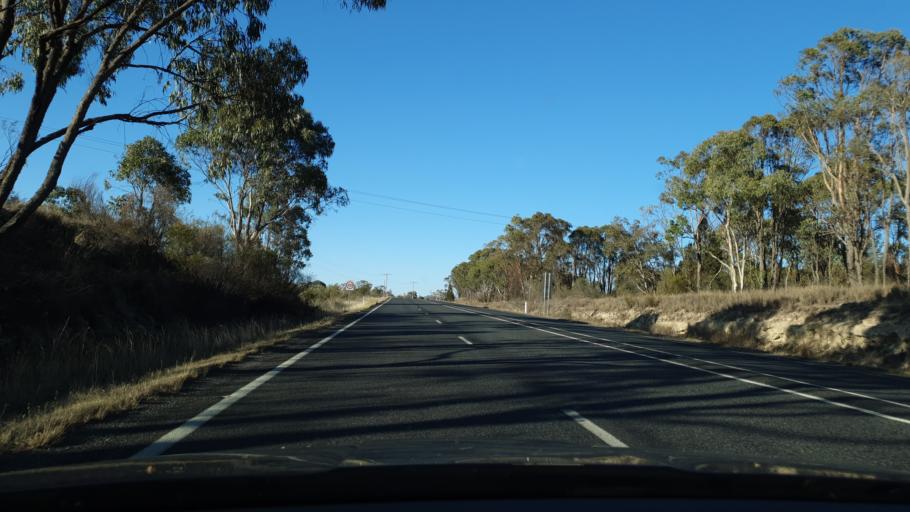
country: AU
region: Queensland
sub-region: Southern Downs
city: Stanthorpe
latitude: -28.6949
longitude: 151.9069
